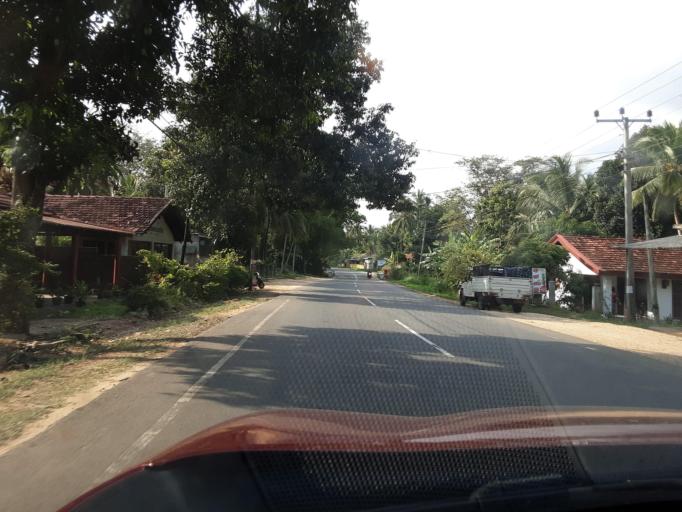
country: LK
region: Uva
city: Haputale
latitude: 6.6774
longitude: 81.1112
